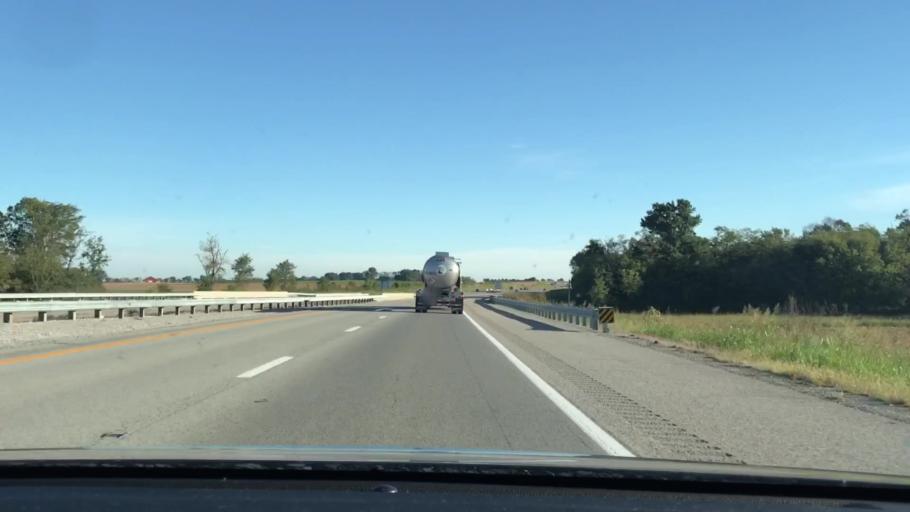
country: US
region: Kentucky
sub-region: Christian County
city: Oak Grove
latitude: 36.7533
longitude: -87.5080
